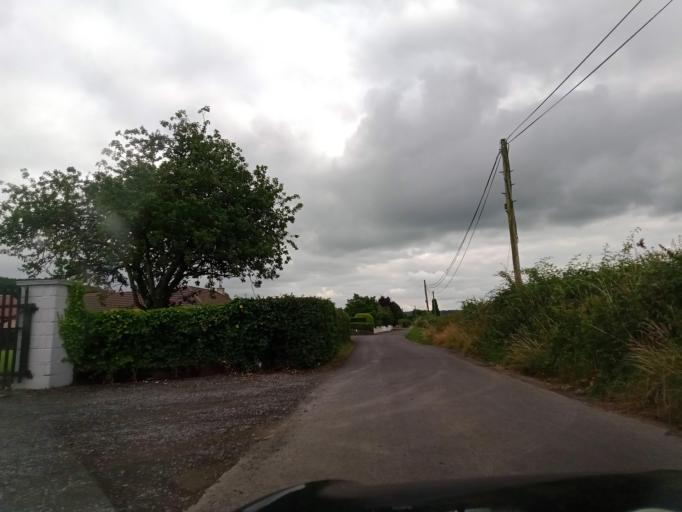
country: IE
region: Leinster
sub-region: Laois
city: Stradbally
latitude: 52.9739
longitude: -7.1555
